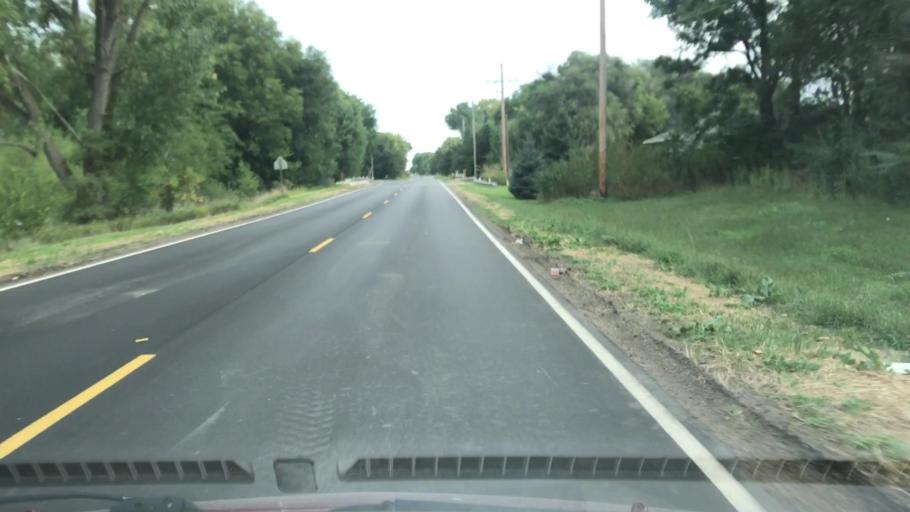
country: US
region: Nebraska
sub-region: Hall County
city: Grand Island
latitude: 40.9199
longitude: -98.3017
